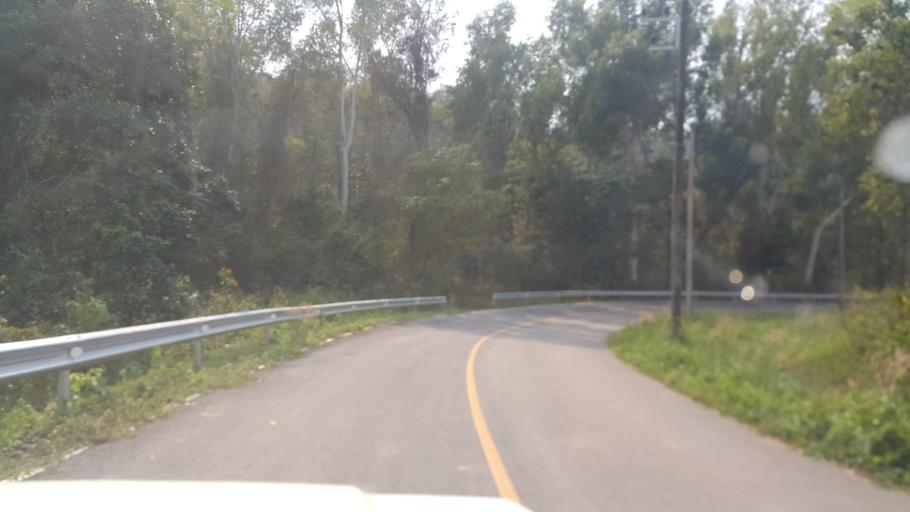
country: TH
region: Nakhon Phanom
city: Ban Phaeng
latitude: 17.9509
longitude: 104.1631
